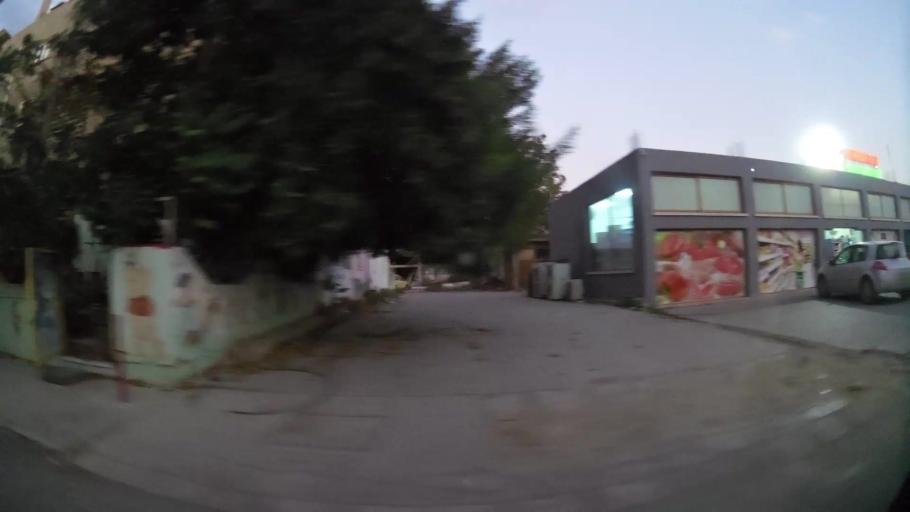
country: CY
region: Lefkosia
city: Nicosia
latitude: 35.1996
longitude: 33.3750
